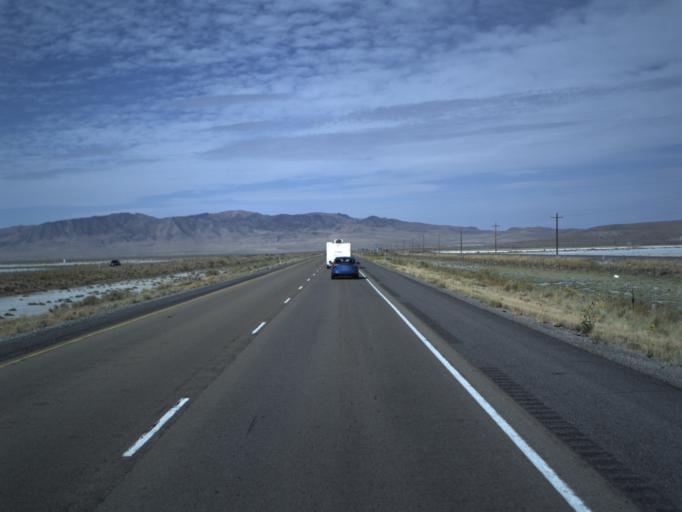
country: US
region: Utah
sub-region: Tooele County
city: Grantsville
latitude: 40.7523
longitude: -112.7149
